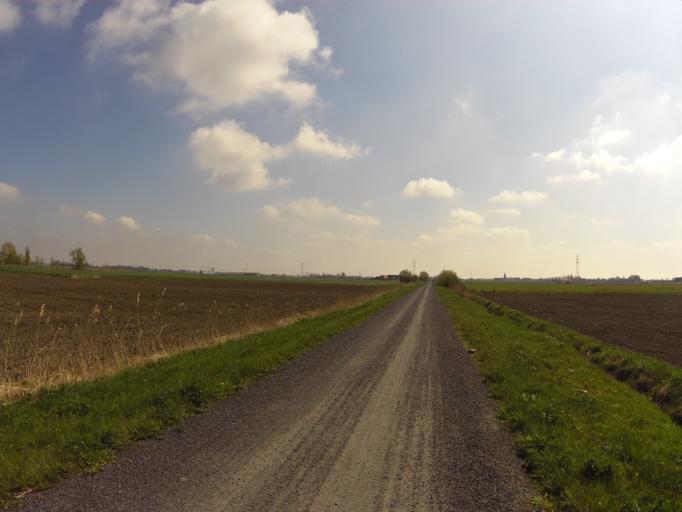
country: BE
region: Flanders
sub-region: Provincie West-Vlaanderen
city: Nieuwpoort
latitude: 51.0870
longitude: 2.7877
